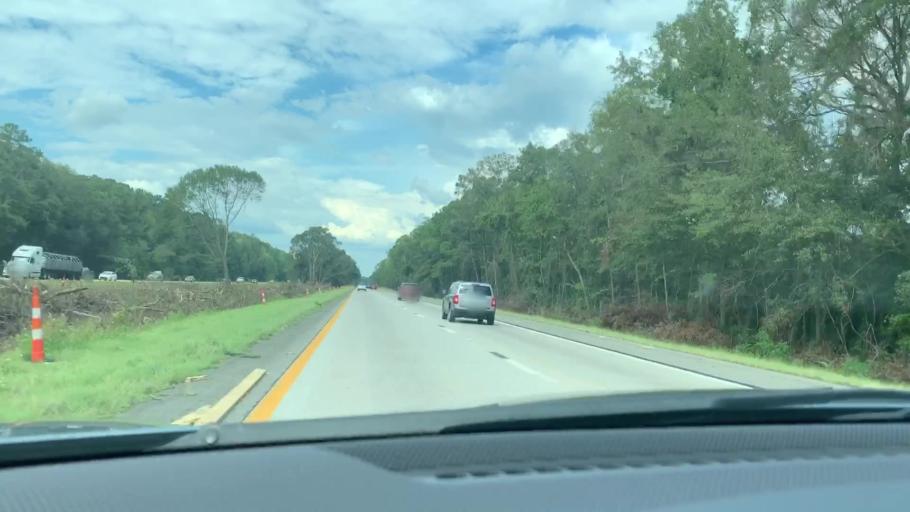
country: US
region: South Carolina
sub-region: Jasper County
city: Ridgeland
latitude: 32.4002
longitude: -81.0190
